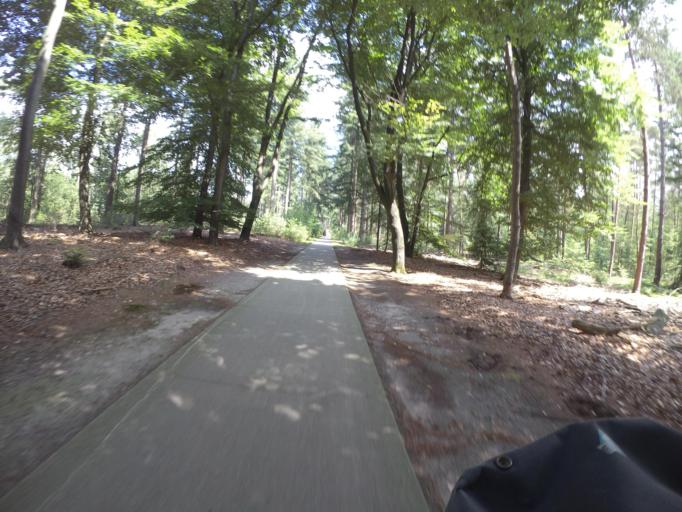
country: NL
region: Gelderland
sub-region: Gemeente Heerde
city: Heerde
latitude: 52.4157
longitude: 6.0236
